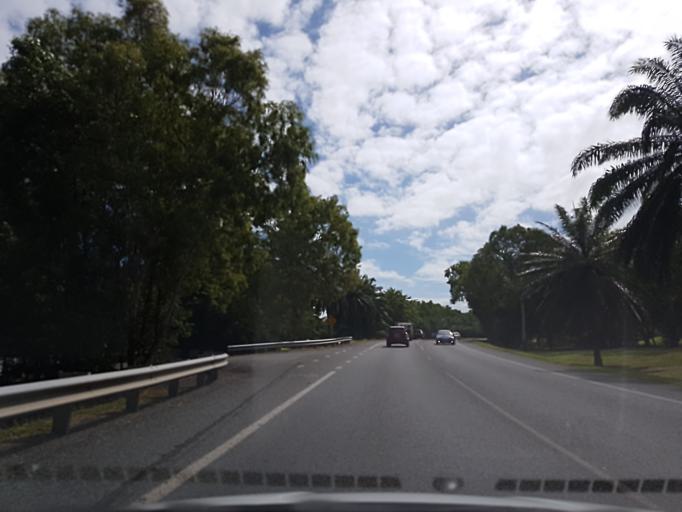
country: AU
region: Queensland
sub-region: Cairns
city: Port Douglas
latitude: -16.5081
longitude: 145.4628
